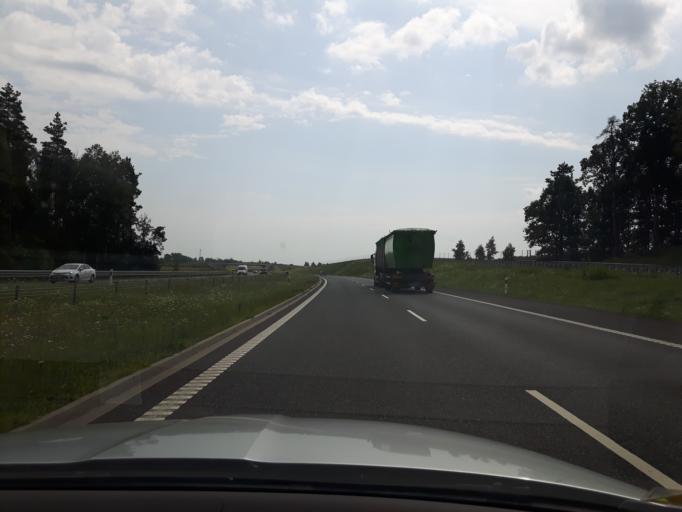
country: PL
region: Warmian-Masurian Voivodeship
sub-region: Powiat olsztynski
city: Olsztynek
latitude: 53.4554
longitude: 20.3215
